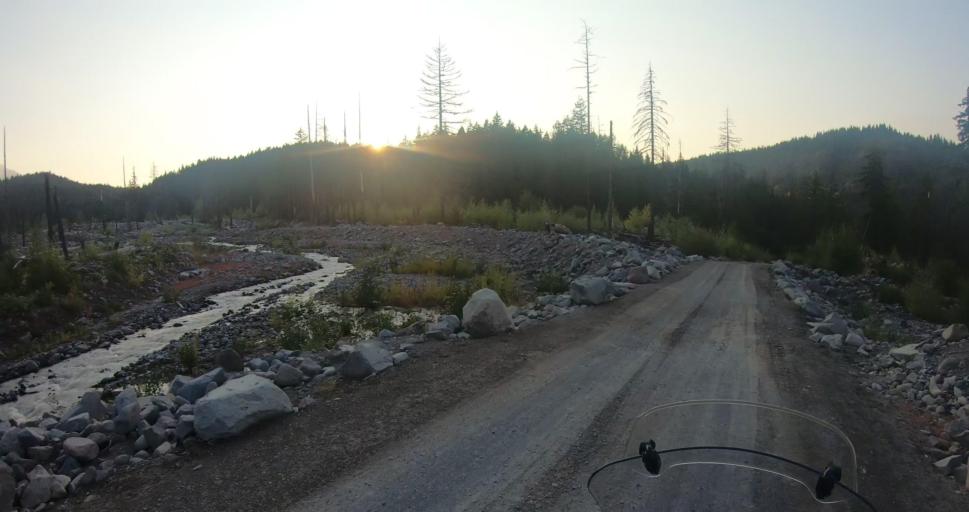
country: US
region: Oregon
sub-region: Hood River County
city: Odell
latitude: 45.4605
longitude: -121.6335
